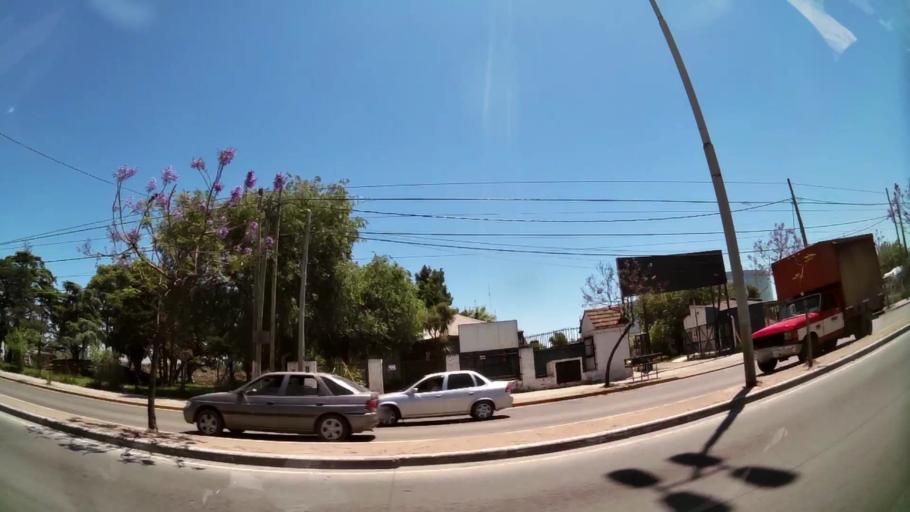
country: AR
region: Buenos Aires
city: Hurlingham
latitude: -34.4981
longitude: -58.7091
